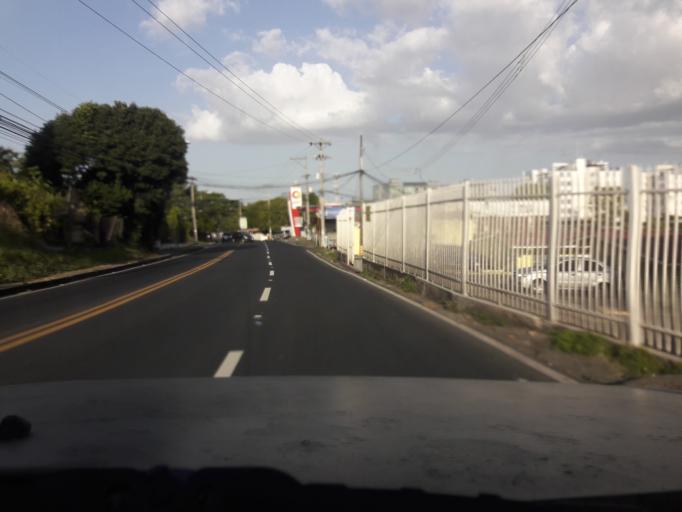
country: PA
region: Panama
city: Panama
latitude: 9.0157
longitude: -79.5051
